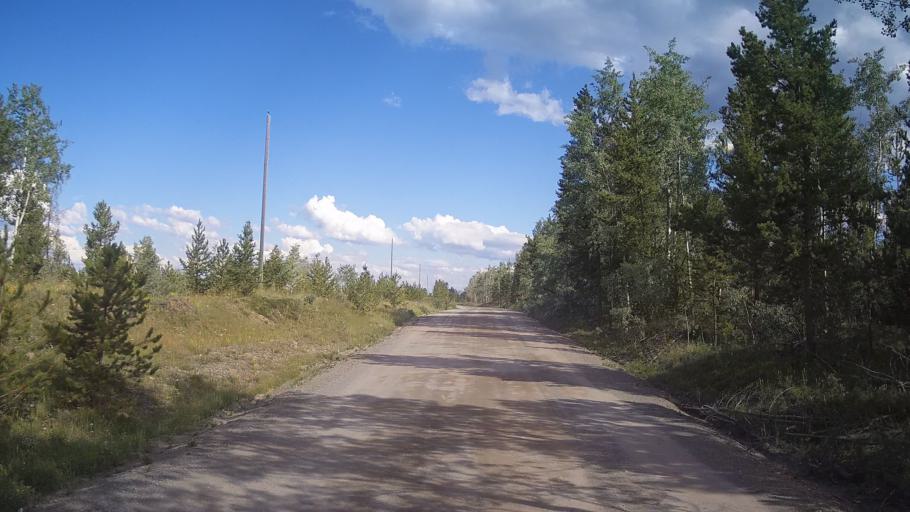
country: CA
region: British Columbia
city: Cache Creek
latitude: 51.2554
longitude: -121.6785
